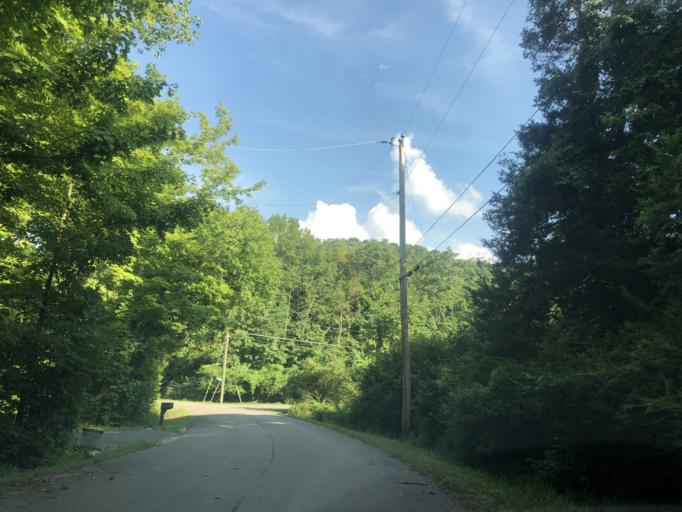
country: US
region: Tennessee
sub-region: Davidson County
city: Nashville
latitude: 36.2399
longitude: -86.8430
